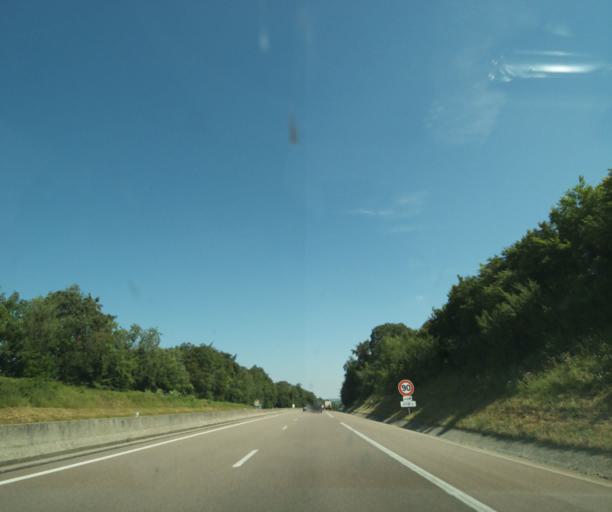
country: FR
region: Lorraine
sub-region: Departement de Meurthe-et-Moselle
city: Colombey-les-Belles
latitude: 48.4236
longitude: 5.8607
